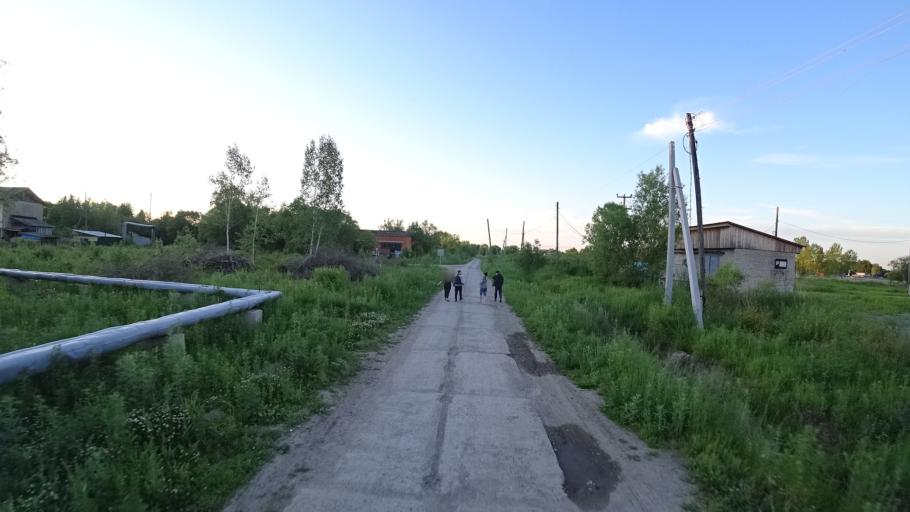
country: RU
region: Khabarovsk Krai
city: Khor
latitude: 47.8481
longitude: 134.9560
